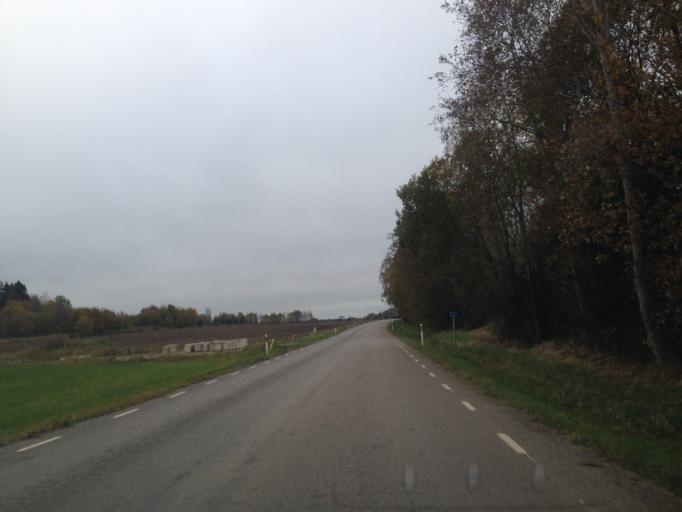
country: EE
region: Harju
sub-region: Saue linn
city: Saue
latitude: 59.3632
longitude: 24.5503
